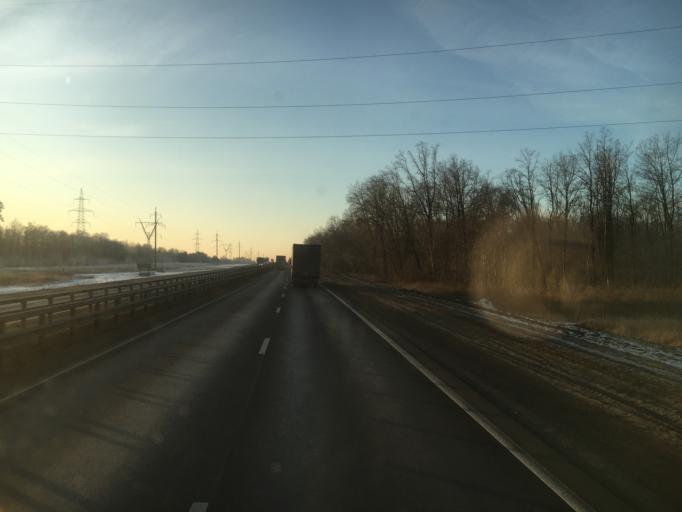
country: RU
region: Samara
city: Pribrezhnyy
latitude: 53.5187
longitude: 49.8169
